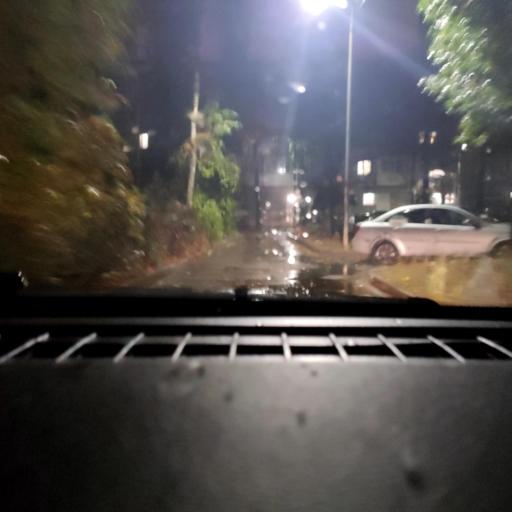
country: RU
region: Voronezj
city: Voronezh
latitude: 51.6475
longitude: 39.1268
